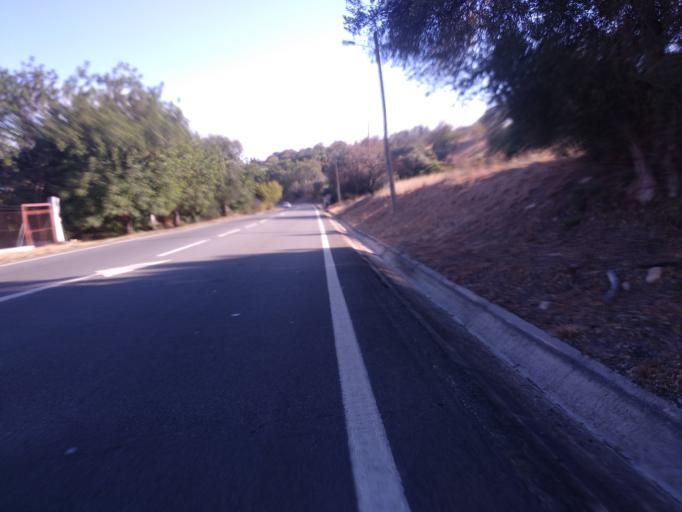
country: PT
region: Faro
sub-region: Sao Bras de Alportel
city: Sao Bras de Alportel
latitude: 37.1096
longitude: -7.9083
